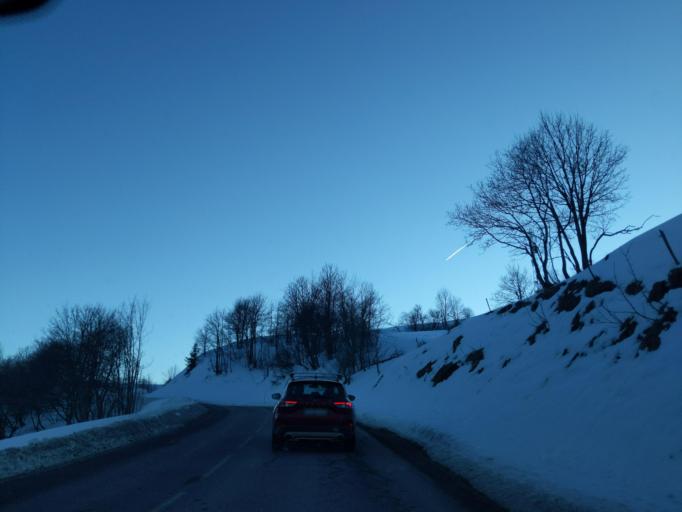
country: FR
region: Rhone-Alpes
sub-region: Departement de la Savoie
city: Saint-Jean-de-Maurienne
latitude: 45.2593
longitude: 6.2747
